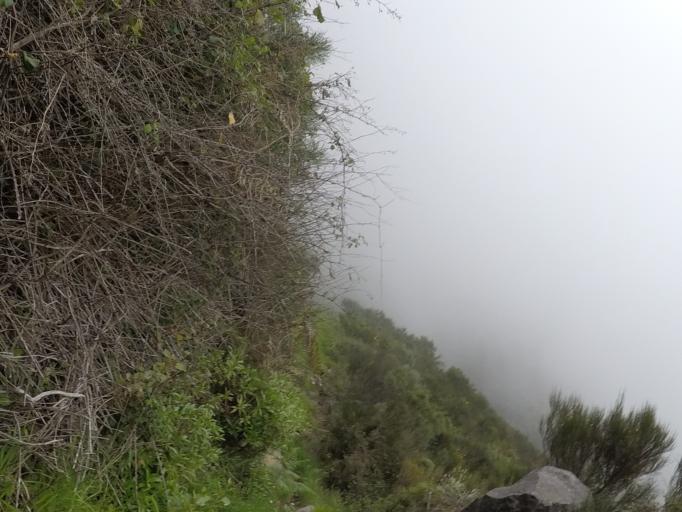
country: PT
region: Madeira
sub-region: Camara de Lobos
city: Curral das Freiras
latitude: 32.7335
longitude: -16.9889
